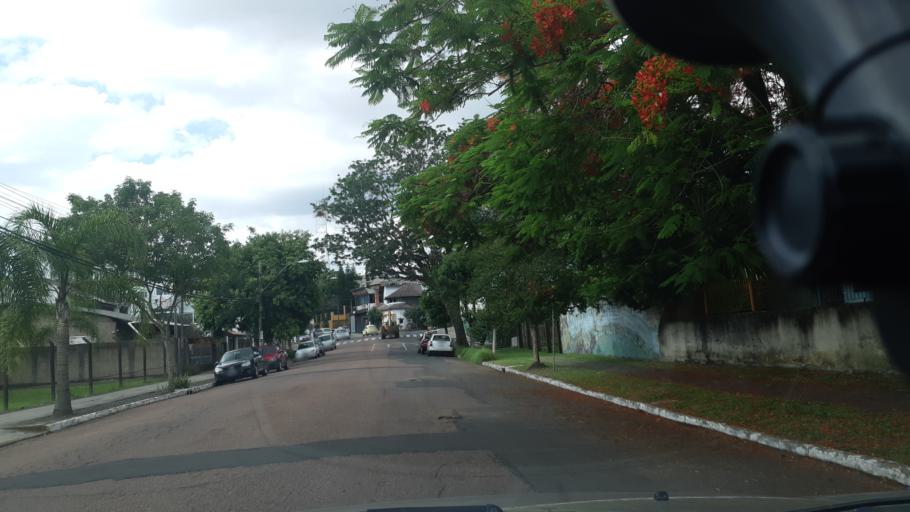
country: BR
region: Rio Grande do Sul
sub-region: Esteio
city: Esteio
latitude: -29.8500
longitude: -51.1680
